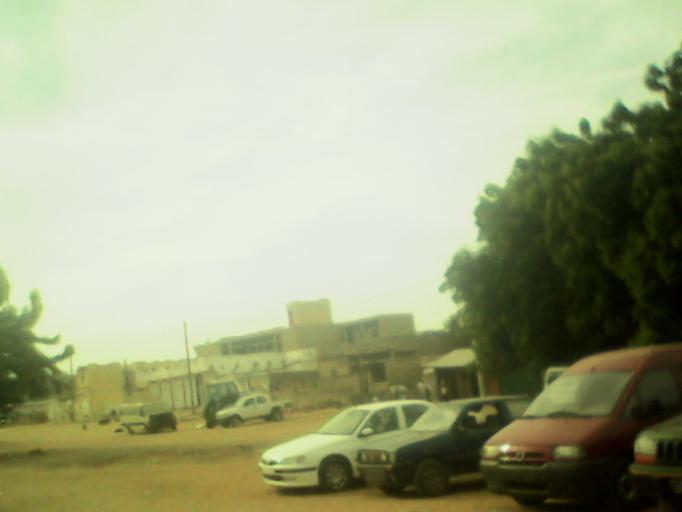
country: SN
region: Diourbel
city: Touba
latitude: 14.8823
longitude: -15.8869
